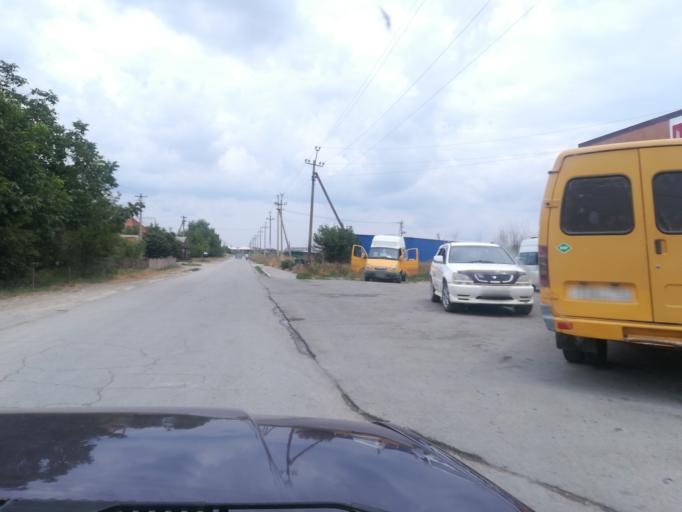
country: RU
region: Krasnodarskiy
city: Vityazevo
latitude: 45.0126
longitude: 37.2934
